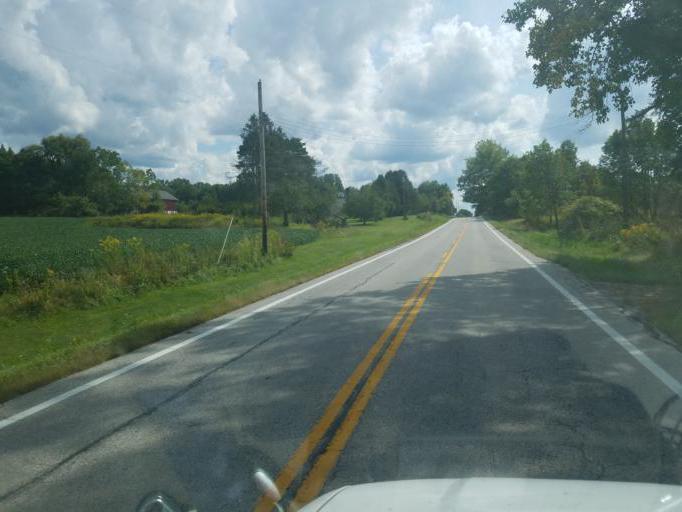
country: US
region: Ohio
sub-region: Portage County
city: Hiram
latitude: 41.3556
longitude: -81.1431
